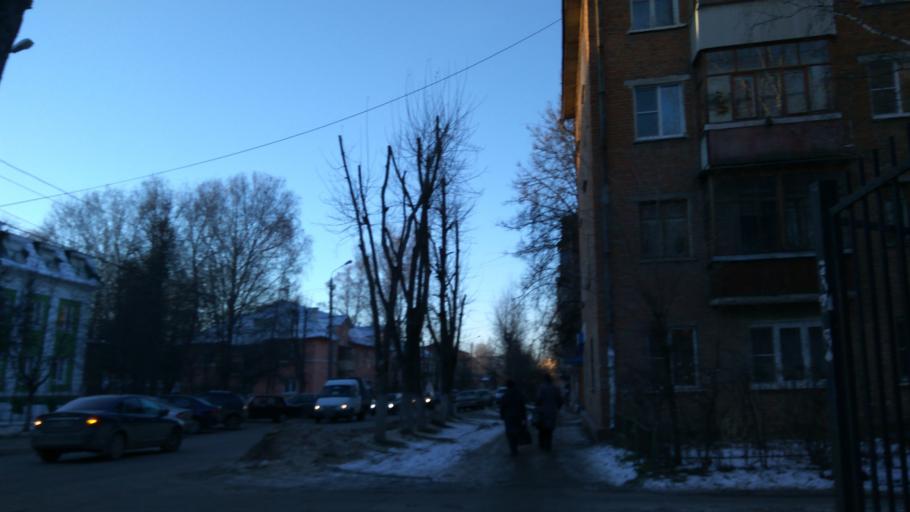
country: RU
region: Tula
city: Mendeleyevskiy
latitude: 54.1709
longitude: 37.5879
